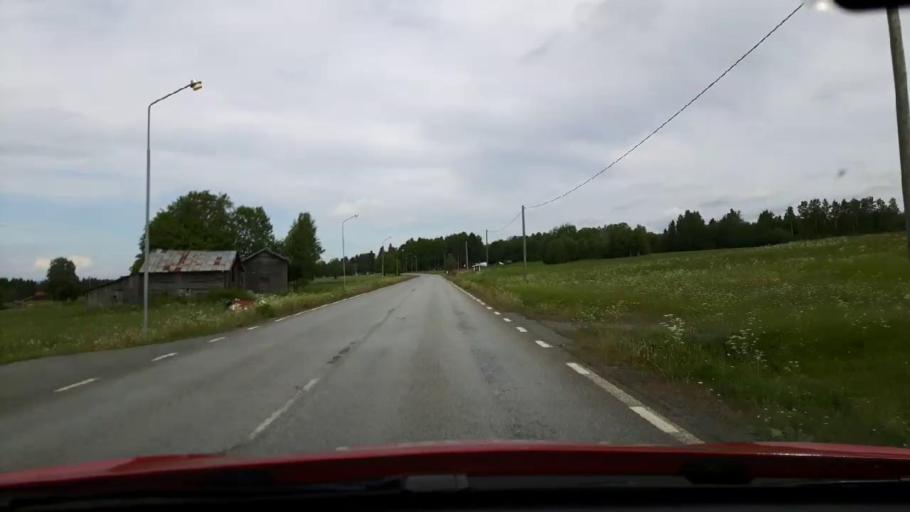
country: SE
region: Jaemtland
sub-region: Bergs Kommun
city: Hoverberg
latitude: 63.0145
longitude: 14.4910
